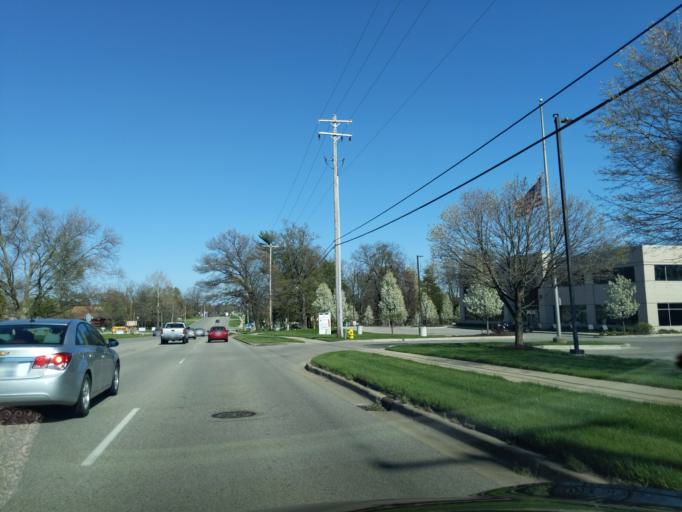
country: US
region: Michigan
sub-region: Kent County
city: East Grand Rapids
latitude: 42.9468
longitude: -85.5613
